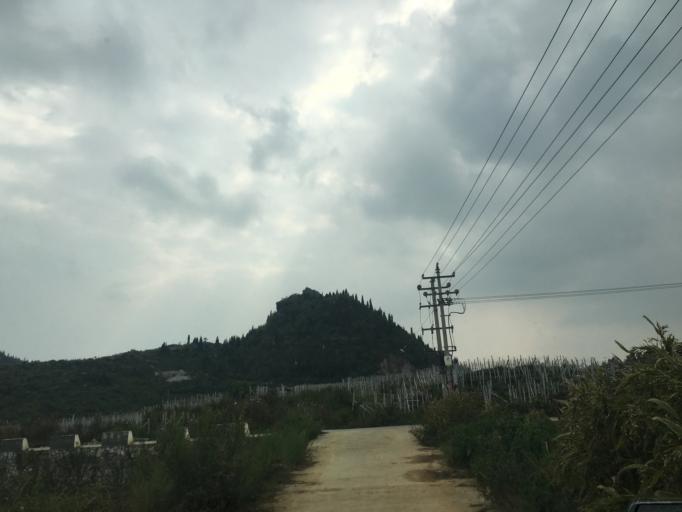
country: CN
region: Guangxi Zhuangzu Zizhiqu
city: Xinzhou
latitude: 25.4848
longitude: 105.6480
